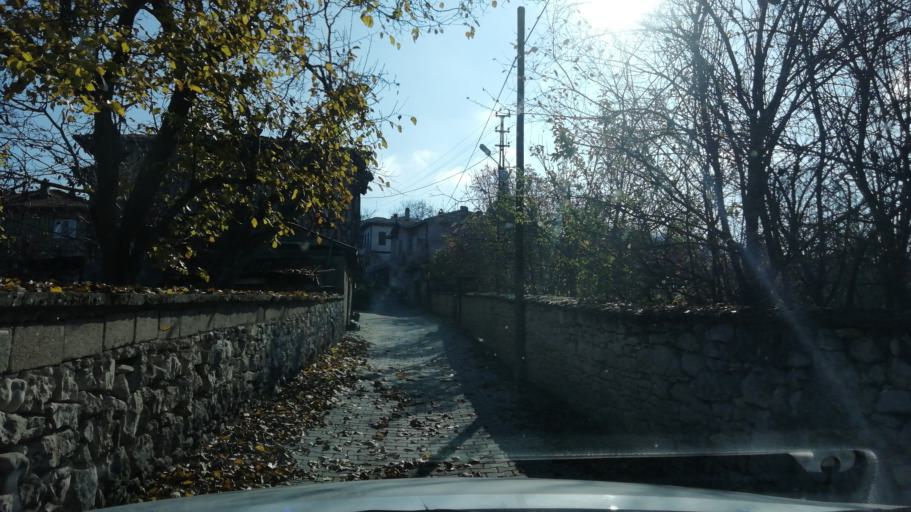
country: TR
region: Karabuk
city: Safranbolu
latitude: 41.2323
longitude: 32.7786
